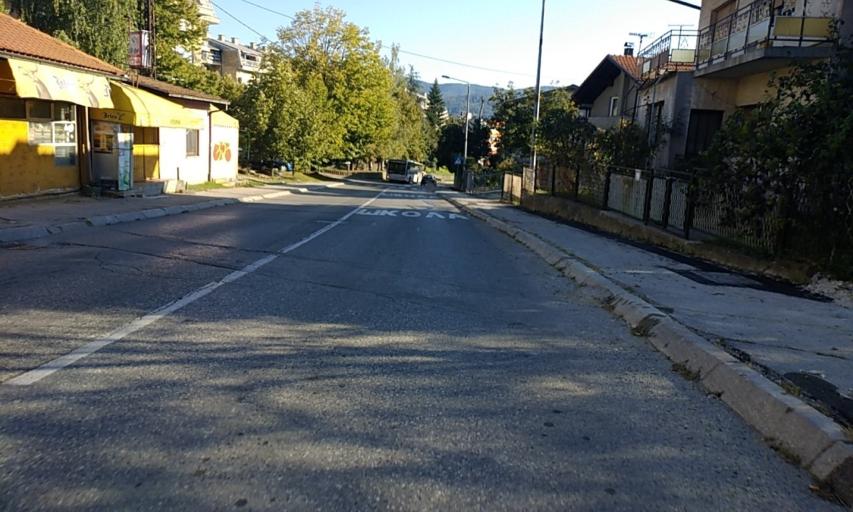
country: BA
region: Republika Srpska
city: Banja Luka
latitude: 44.7758
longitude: 17.1781
